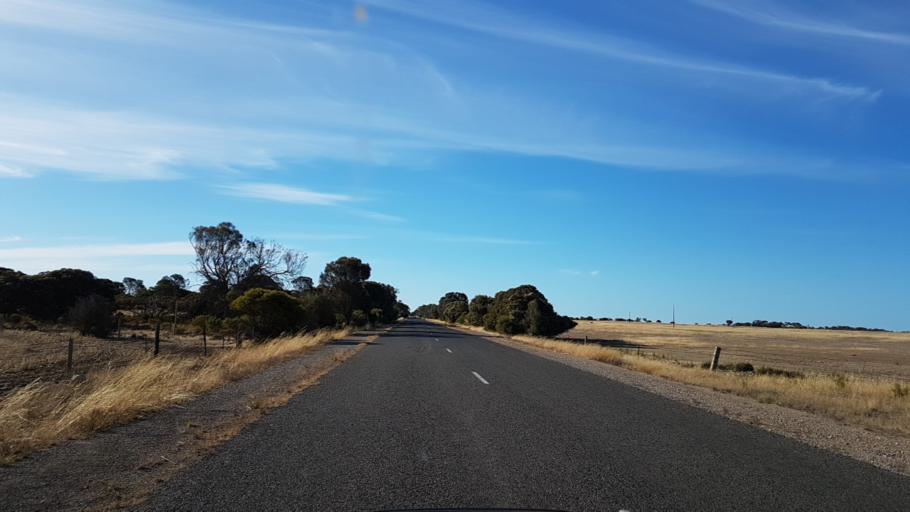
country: AU
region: South Australia
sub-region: Yorke Peninsula
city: Honiton
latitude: -34.9376
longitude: 137.0910
